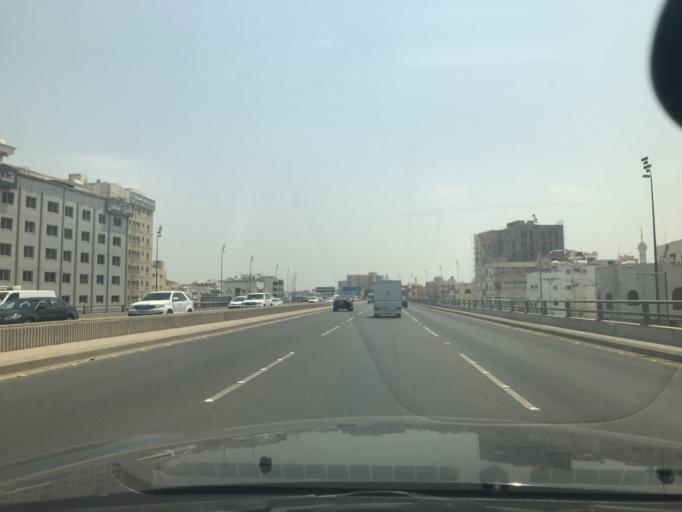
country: SA
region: Makkah
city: Jeddah
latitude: 21.4772
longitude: 39.1869
